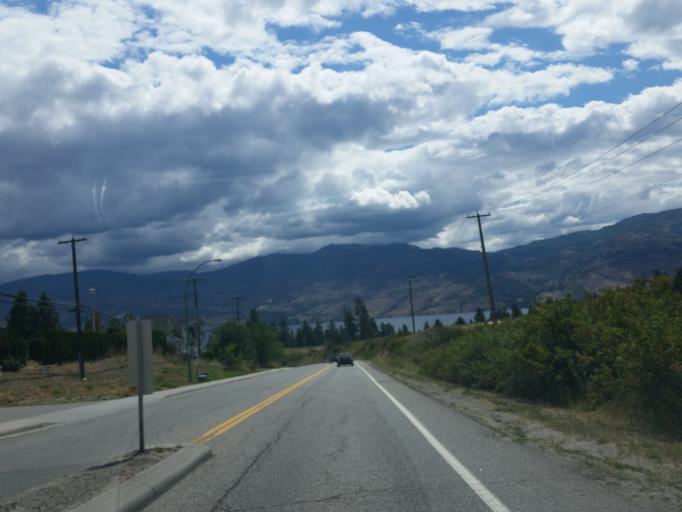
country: CA
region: British Columbia
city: West Kelowna
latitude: 49.8293
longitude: -119.6209
